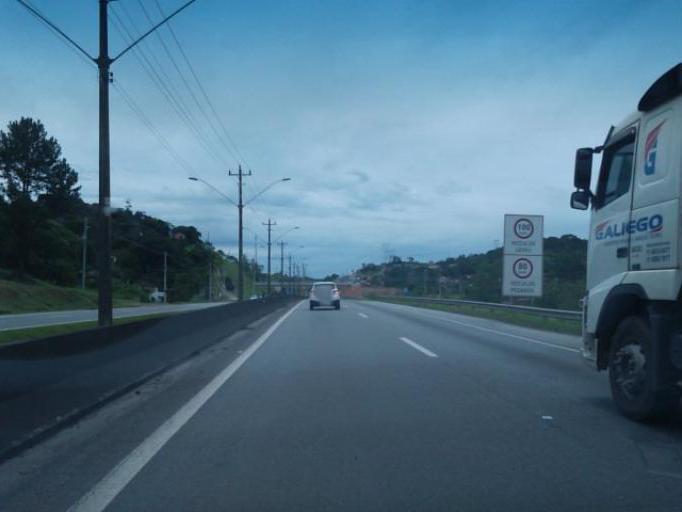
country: BR
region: Sao Paulo
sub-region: Sao Lourenco Da Serra
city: Sao Lourenco da Serra
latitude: -23.8802
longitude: -46.9706
